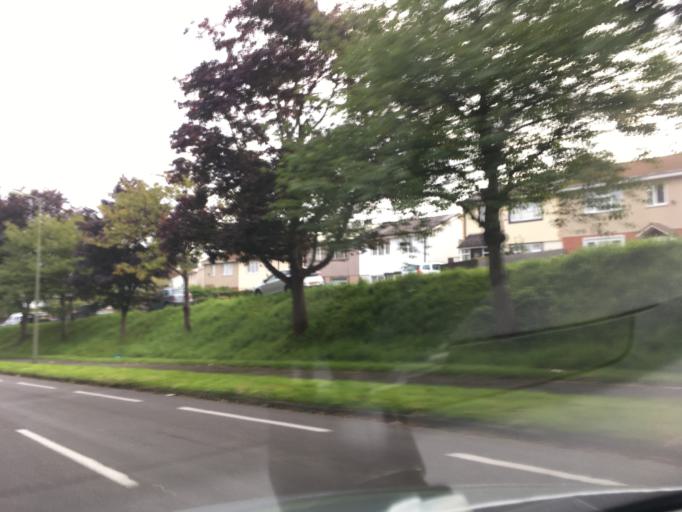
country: GB
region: England
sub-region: Oxfordshire
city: Cowley
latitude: 51.7654
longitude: -1.1931
